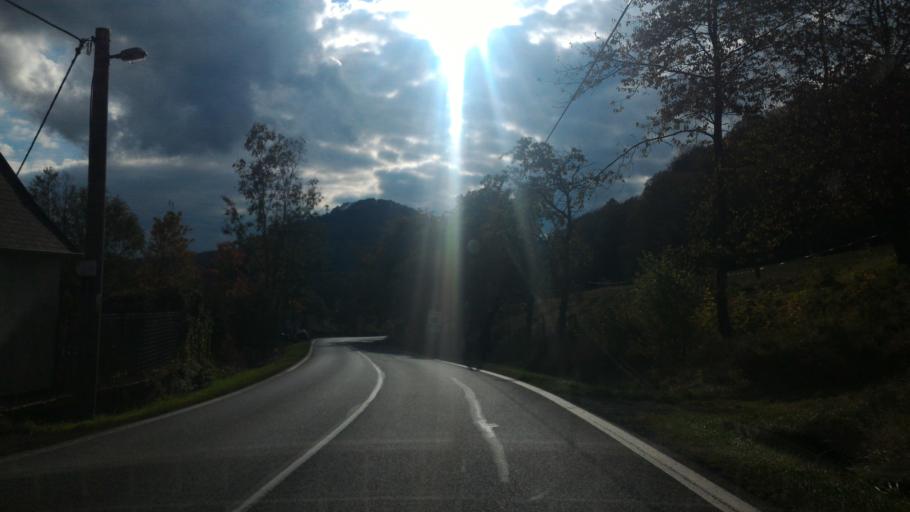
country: CZ
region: Ustecky
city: Ceska Kamenice
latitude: 50.8045
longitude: 14.4422
